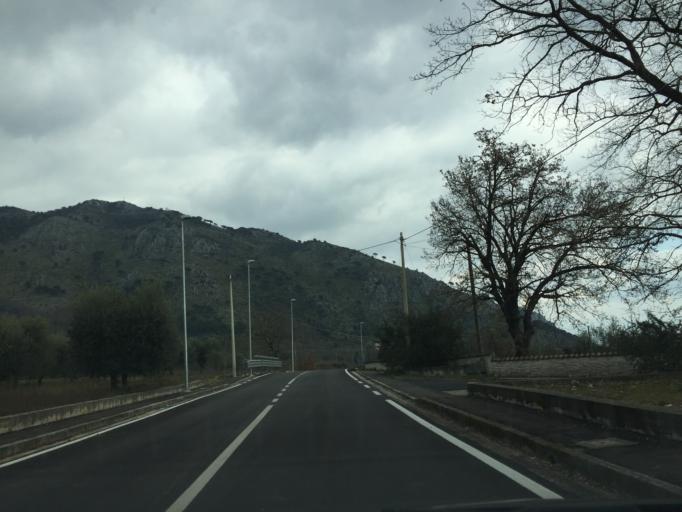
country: IT
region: Latium
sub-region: Provincia di Frosinone
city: Villa Santa Lucia
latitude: 41.4950
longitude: 13.7724
